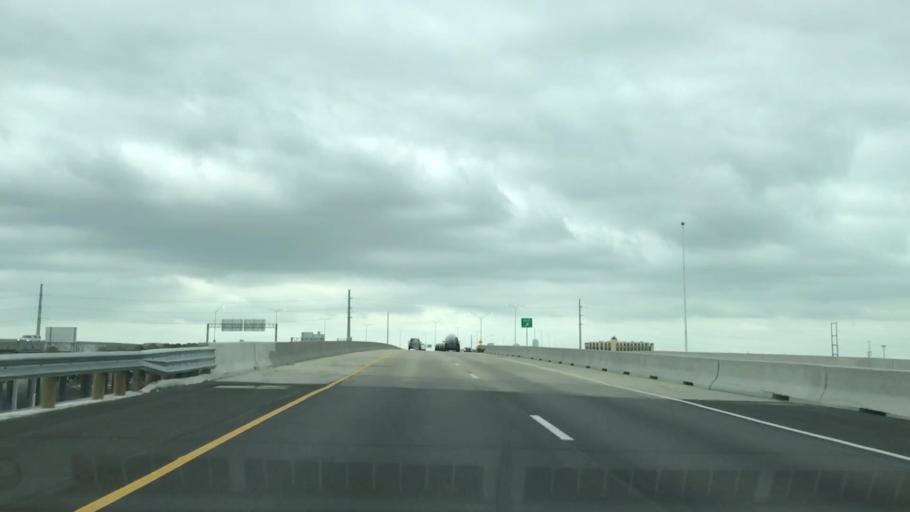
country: US
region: Texas
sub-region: Dallas County
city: Irving
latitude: 32.8336
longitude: -96.8966
